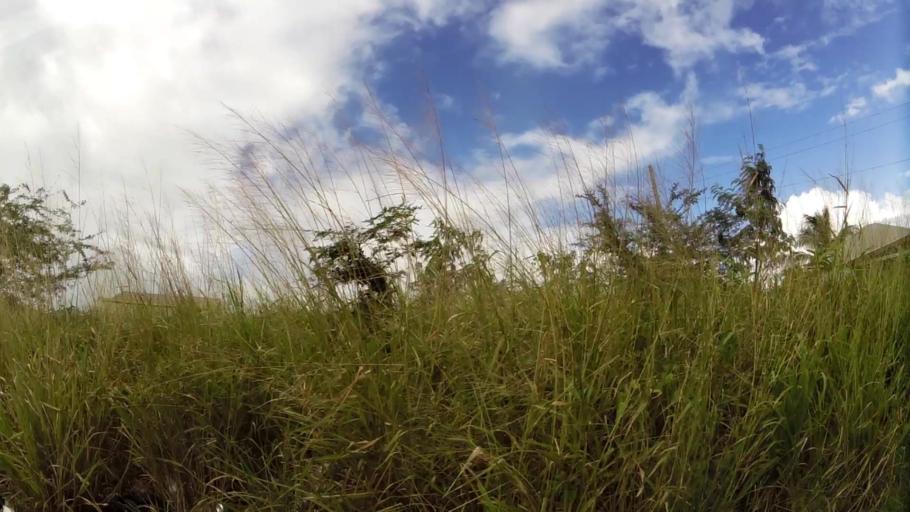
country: AG
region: Saint George
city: Piggotts
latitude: 17.1056
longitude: -61.8078
